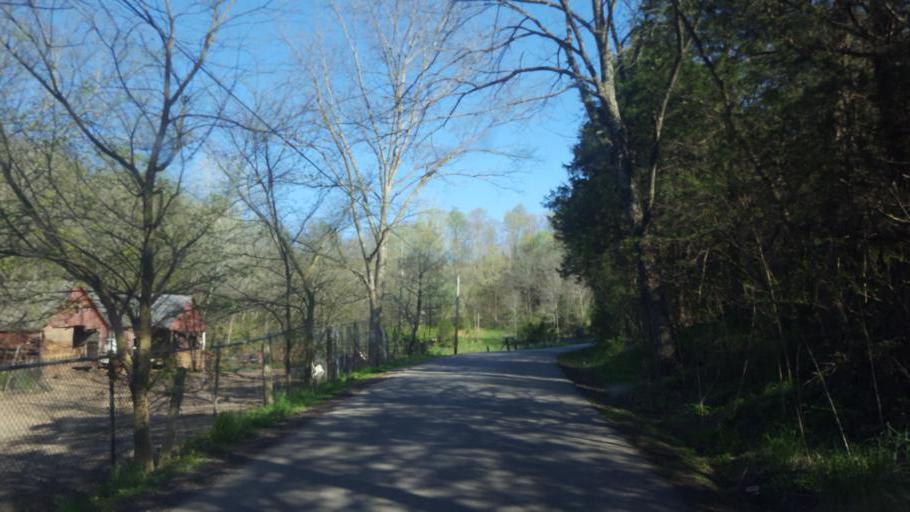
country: US
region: Kentucky
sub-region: Barren County
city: Cave City
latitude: 37.1765
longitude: -86.0027
